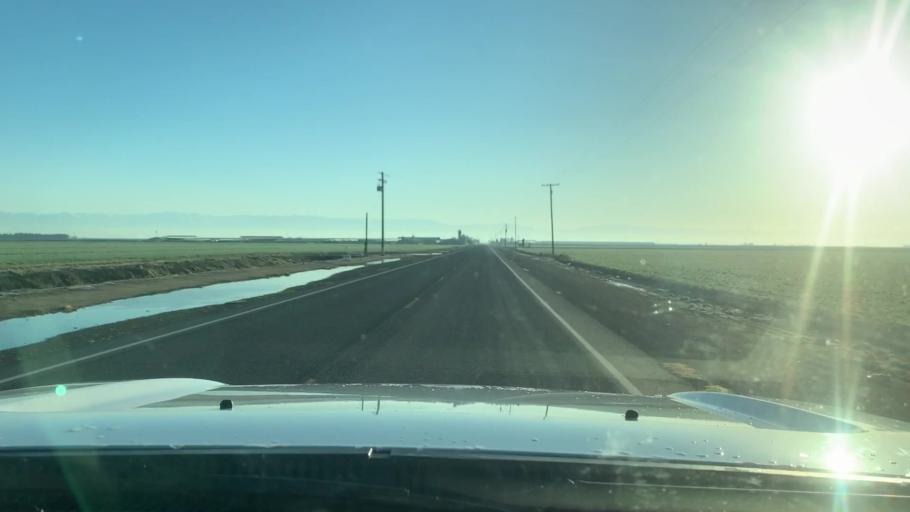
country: US
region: California
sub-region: Kings County
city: Corcoran
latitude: 36.2111
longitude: -119.5555
